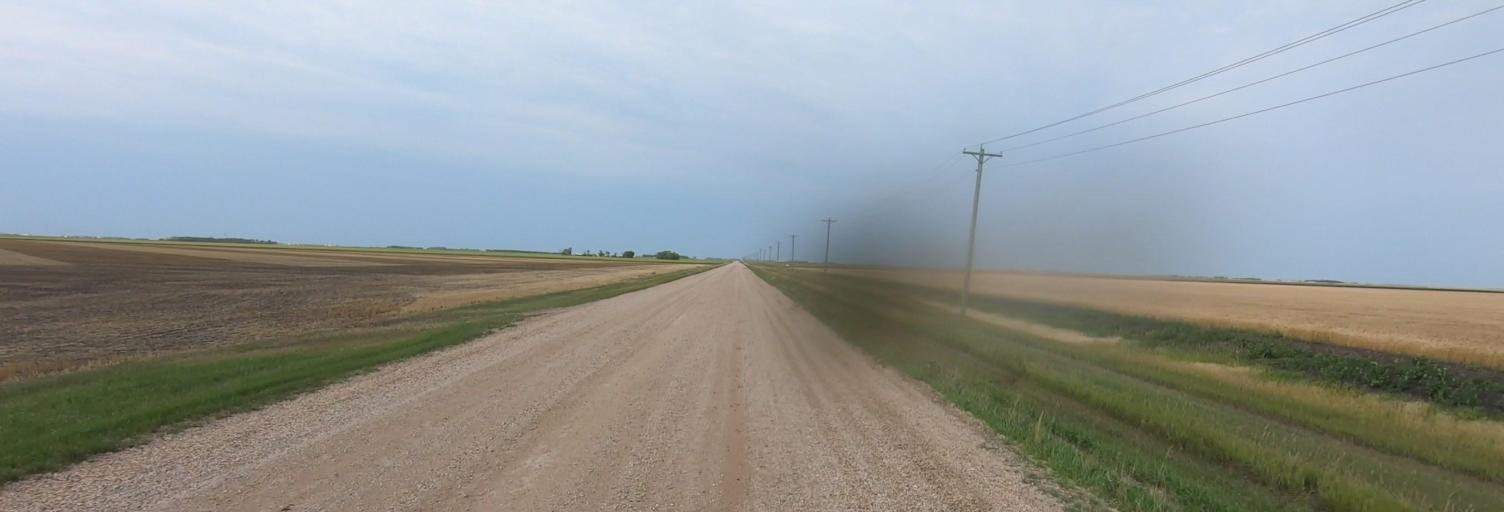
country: CA
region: Manitoba
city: Niverville
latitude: 49.5765
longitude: -97.2690
